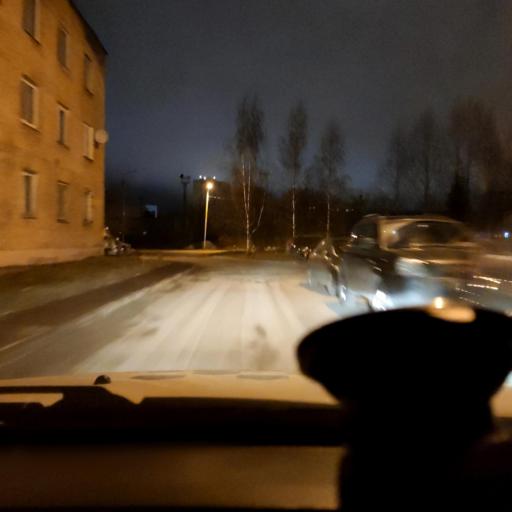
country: RU
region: Perm
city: Perm
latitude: 57.9695
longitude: 56.1938
